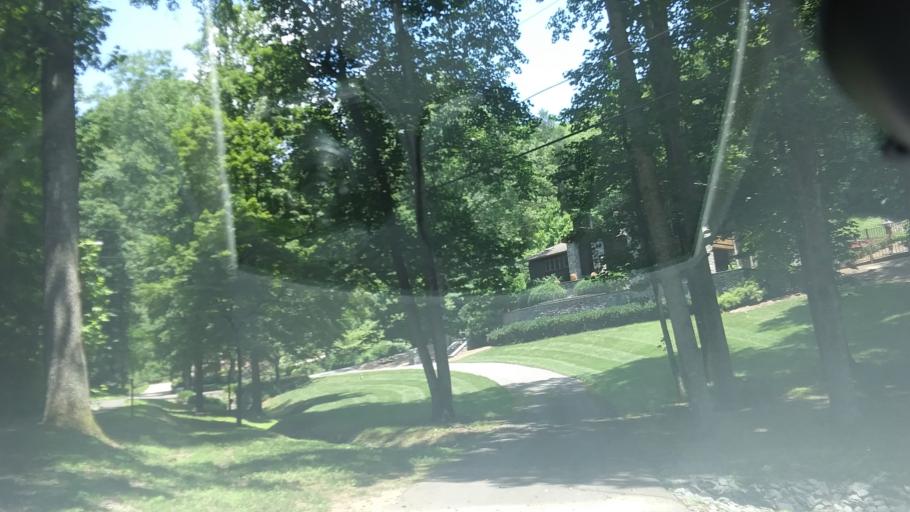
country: US
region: Tennessee
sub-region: Davidson County
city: Belle Meade
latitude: 36.0914
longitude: -86.9517
